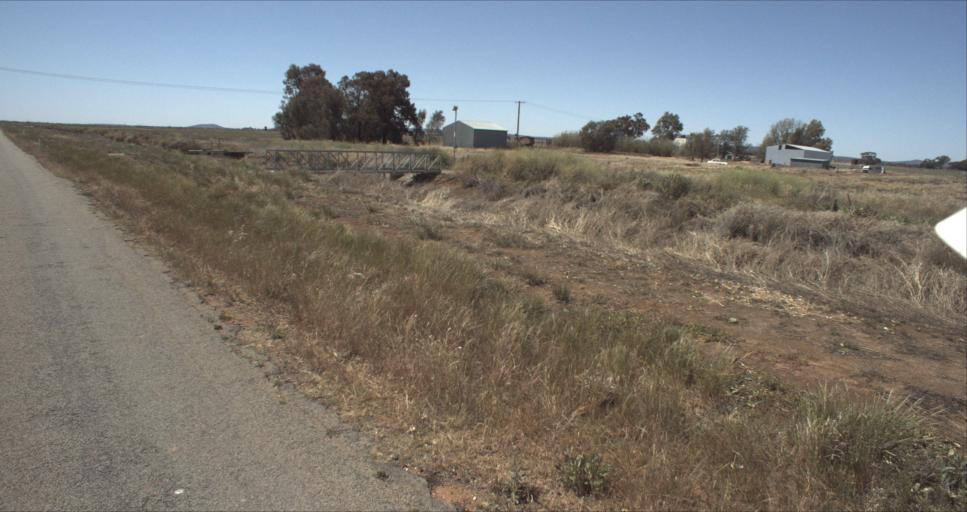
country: AU
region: New South Wales
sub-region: Leeton
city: Leeton
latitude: -34.5054
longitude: 146.3444
